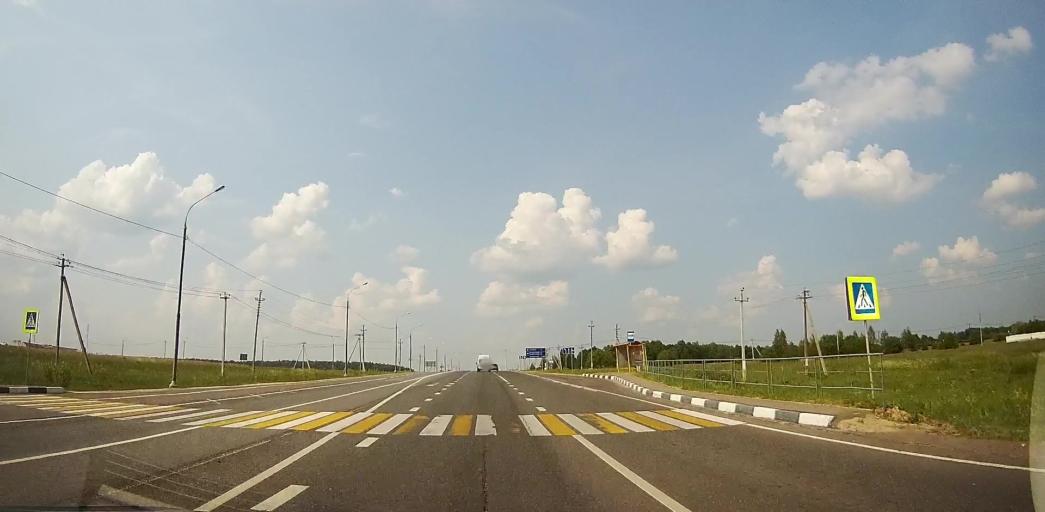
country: RU
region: Moskovskaya
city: Stupino
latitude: 54.9547
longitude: 38.1253
